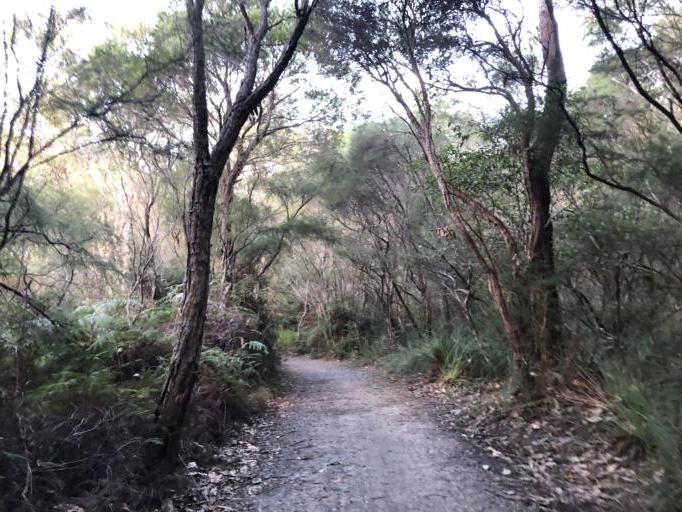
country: AU
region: New South Wales
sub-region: Coffs Harbour
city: Coffs Harbour
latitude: -30.3012
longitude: 153.1314
